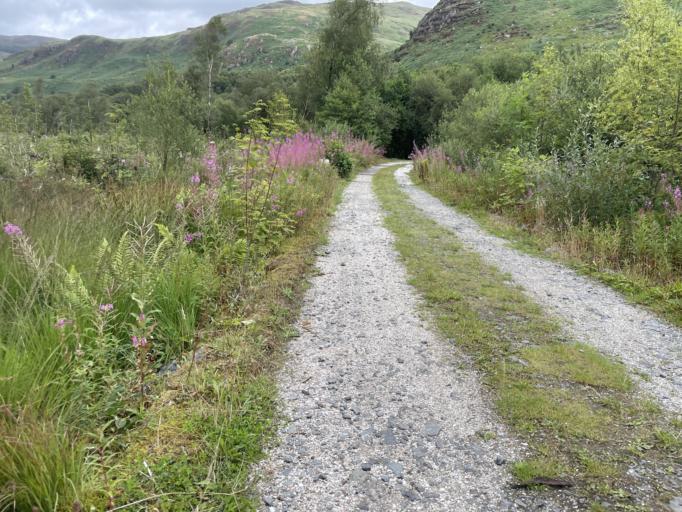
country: GB
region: Scotland
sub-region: Dumfries and Galloway
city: Newton Stewart
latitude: 55.0881
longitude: -4.4582
